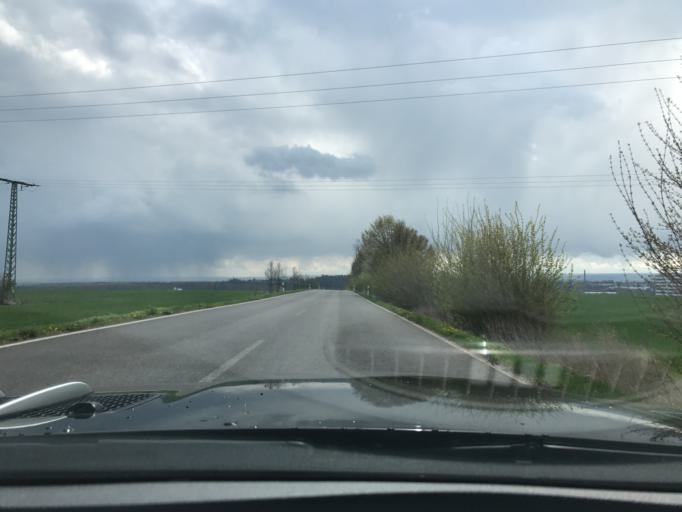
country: DE
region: Thuringia
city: Muehlhausen
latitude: 51.2217
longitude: 10.4921
